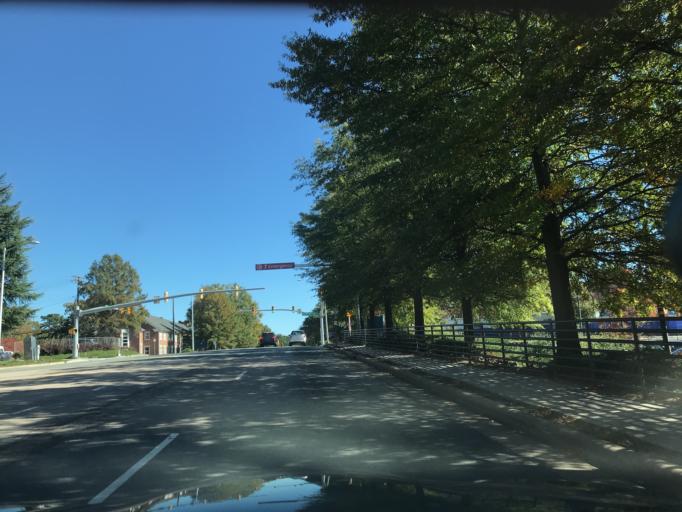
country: US
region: North Carolina
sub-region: Durham County
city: Durham
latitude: 36.0080
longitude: -78.9362
